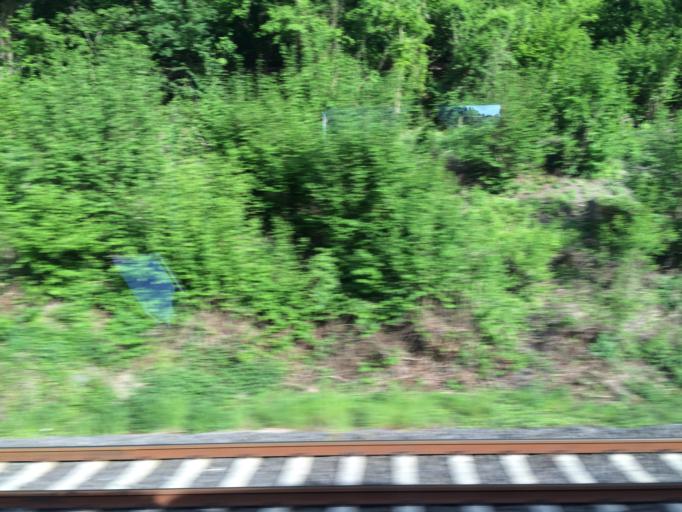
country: DE
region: Rheinland-Pfalz
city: Oberwesel
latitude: 50.1199
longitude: 7.7314
